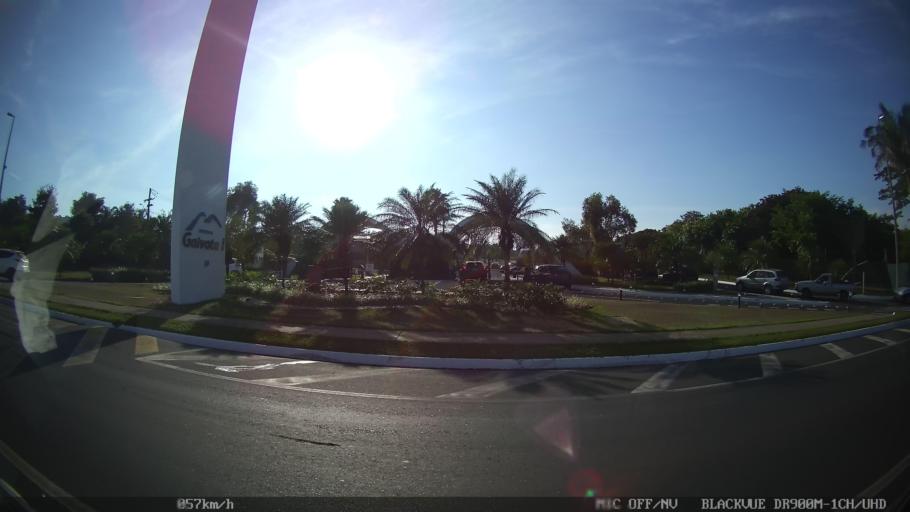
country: BR
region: Sao Paulo
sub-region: Sao Jose Do Rio Preto
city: Sao Jose do Rio Preto
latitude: -20.8063
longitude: -49.3431
